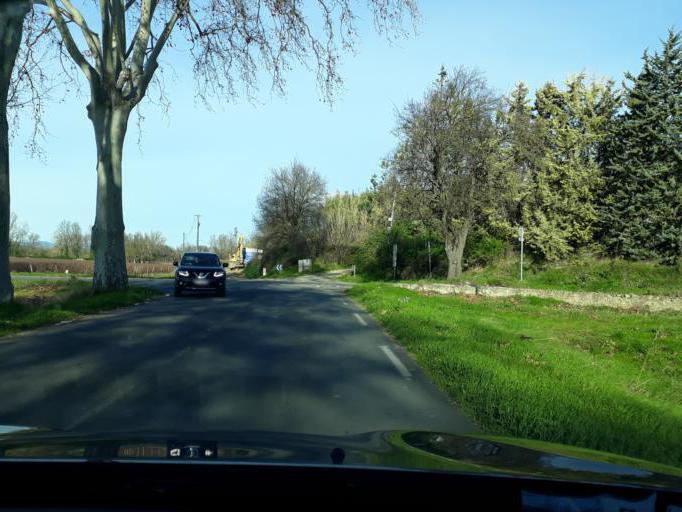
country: FR
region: Languedoc-Roussillon
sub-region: Departement de l'Herault
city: Castelnau-de-Guers
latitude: 43.4459
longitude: 3.4406
